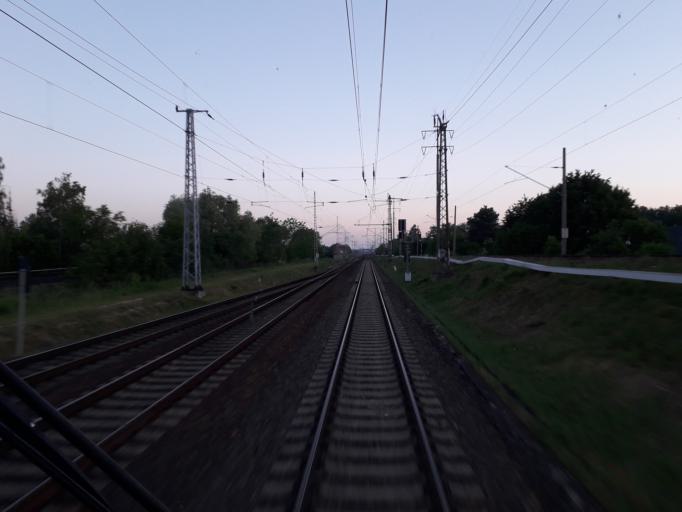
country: DE
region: Berlin
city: Blankenburg
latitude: 52.6102
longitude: 13.4554
